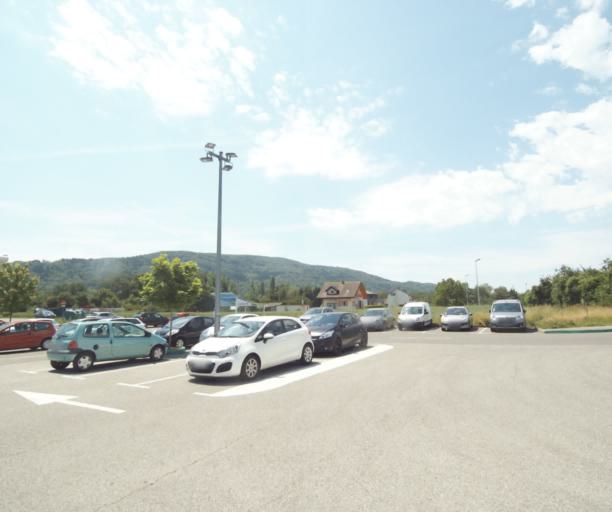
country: FR
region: Rhone-Alpes
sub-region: Departement de la Haute-Savoie
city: Sciez
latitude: 46.3311
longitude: 6.3733
